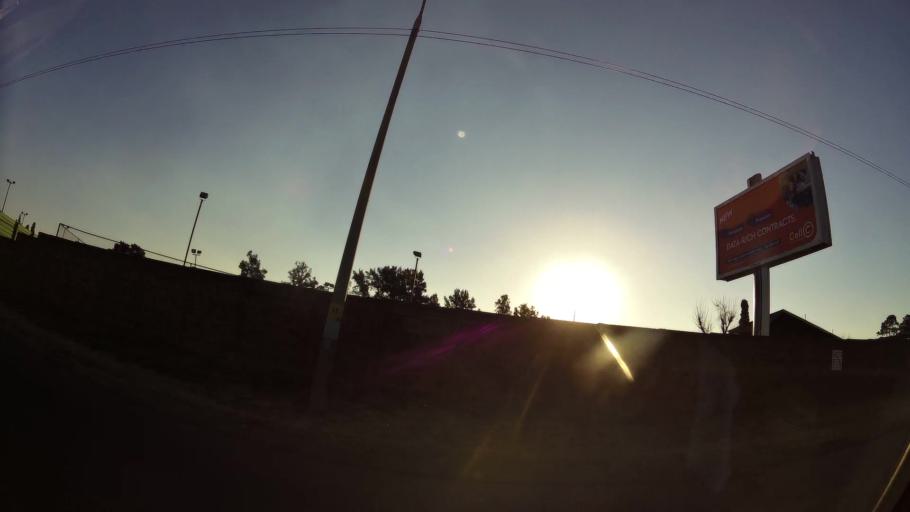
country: ZA
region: Gauteng
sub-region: Ekurhuleni Metropolitan Municipality
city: Germiston
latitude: -26.2678
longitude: 28.1259
